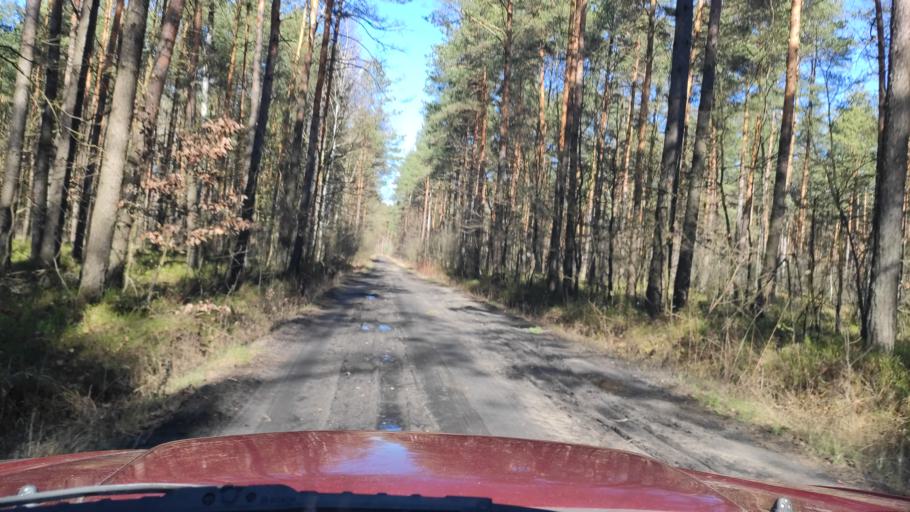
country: PL
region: Masovian Voivodeship
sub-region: Powiat kozienicki
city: Garbatka-Letnisko
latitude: 51.4325
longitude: 21.5474
